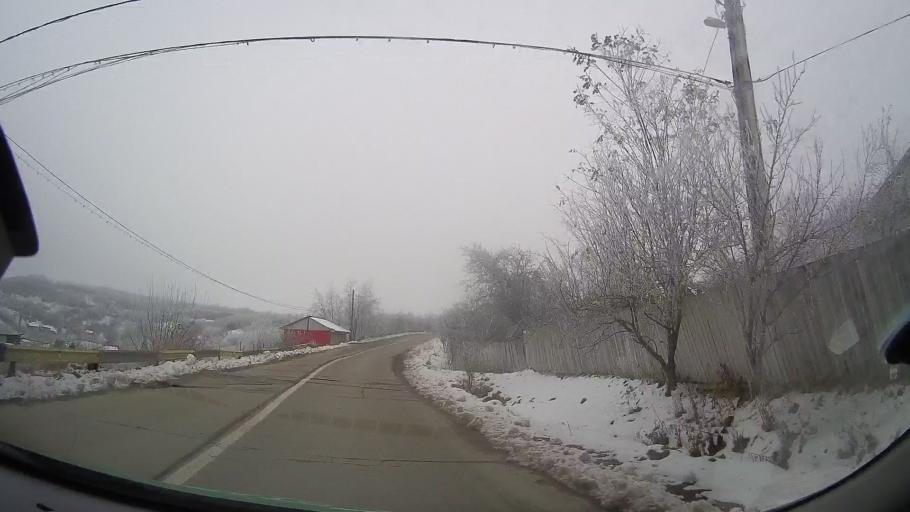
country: RO
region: Vaslui
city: Coroiesti
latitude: 46.2163
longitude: 27.4407
